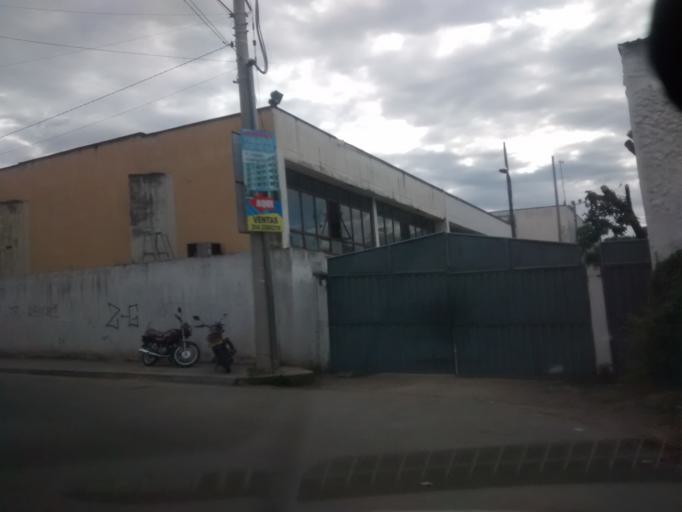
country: CO
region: Cundinamarca
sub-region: Girardot
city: Girardot City
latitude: 4.3058
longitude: -74.8020
